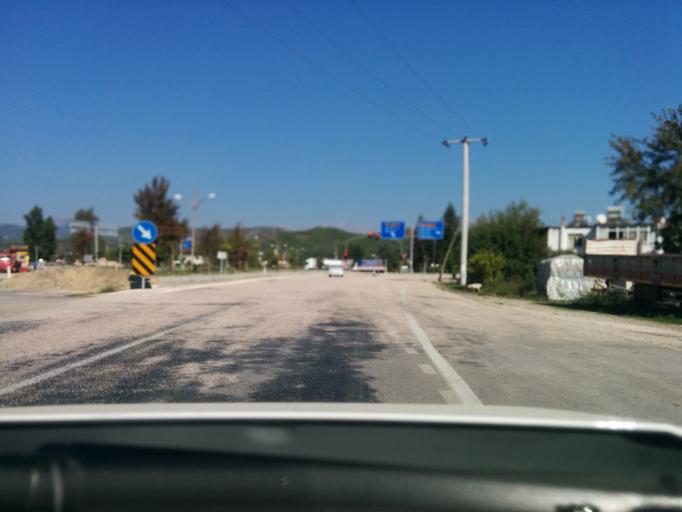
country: TR
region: Mugla
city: Kemer
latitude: 36.6322
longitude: 29.3556
